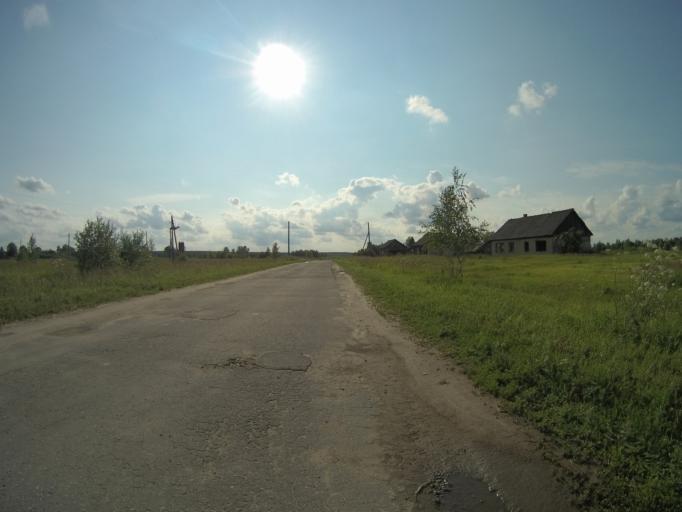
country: RU
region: Vladimir
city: Orgtrud
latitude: 56.3448
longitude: 40.6949
